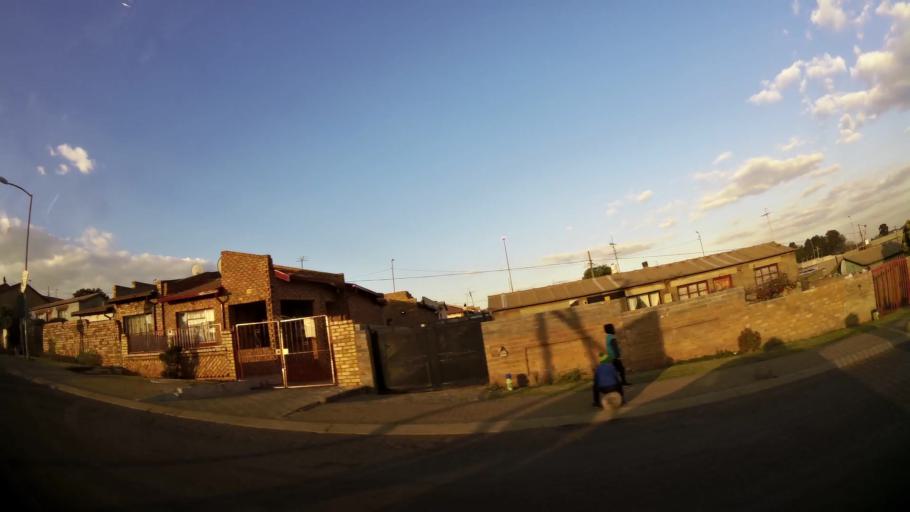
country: ZA
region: Gauteng
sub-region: West Rand District Municipality
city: Krugersdorp
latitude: -26.0812
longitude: 27.7530
